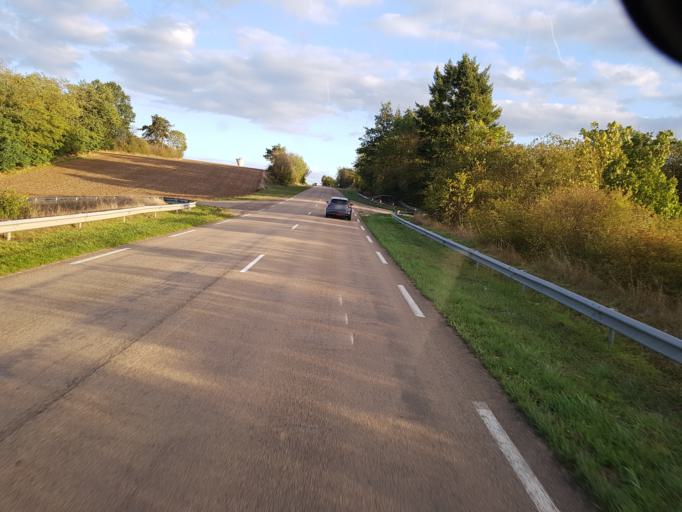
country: FR
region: Bourgogne
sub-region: Departement de l'Yonne
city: Sergines
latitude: 48.3172
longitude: 3.2329
